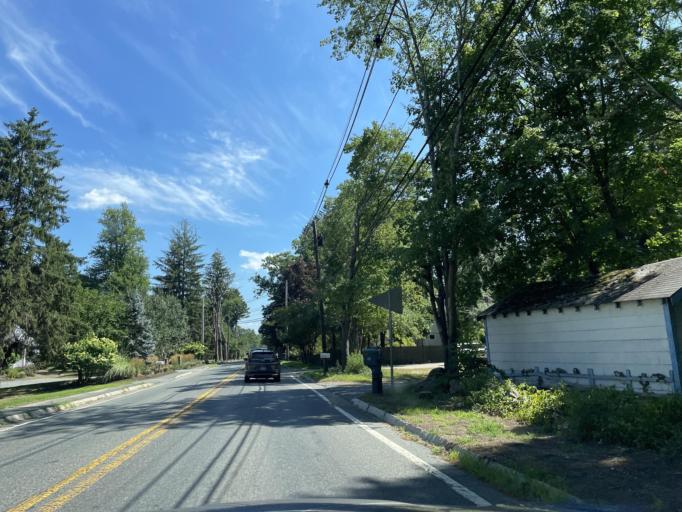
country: US
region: Massachusetts
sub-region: Middlesex County
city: Holliston
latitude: 42.2198
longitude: -71.4272
